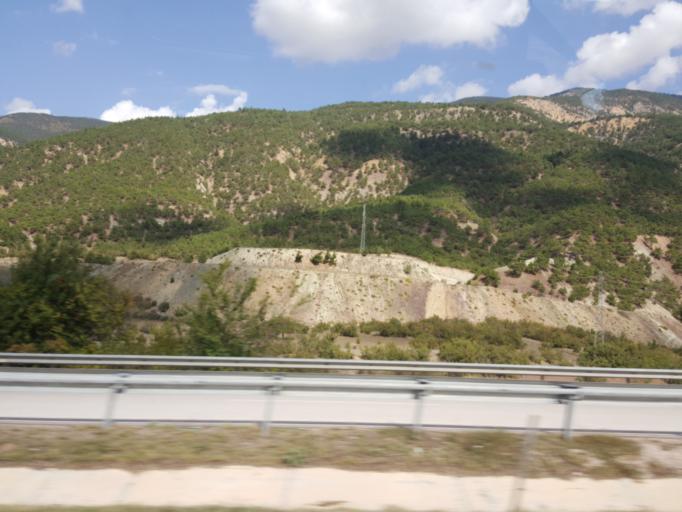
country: TR
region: Sivas
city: Dogansar
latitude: 40.3371
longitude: 37.5325
